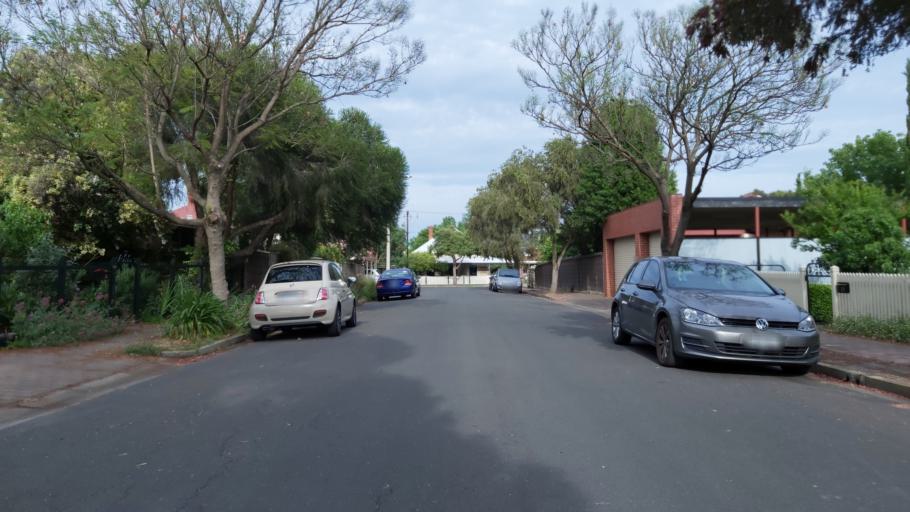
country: AU
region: South Australia
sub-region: Unley
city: Unley
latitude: -34.9530
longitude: 138.5952
